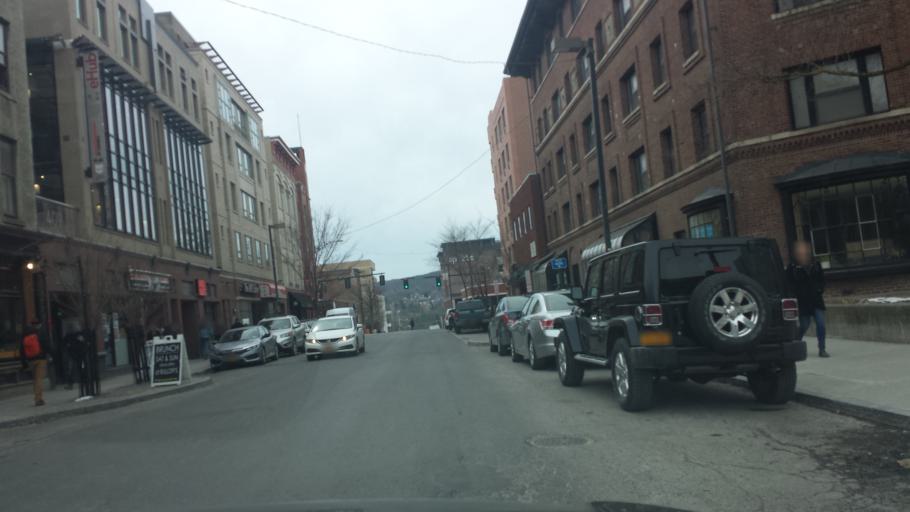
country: US
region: New York
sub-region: Tompkins County
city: East Ithaca
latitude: 42.4424
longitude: -76.4853
